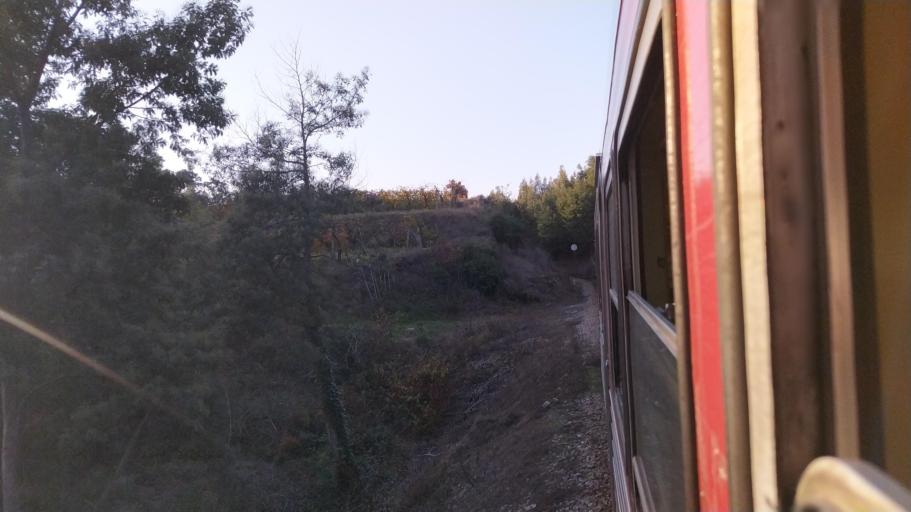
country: PT
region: Aveiro
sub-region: Aveiro
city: Eixo
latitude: 40.6342
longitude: -8.5762
